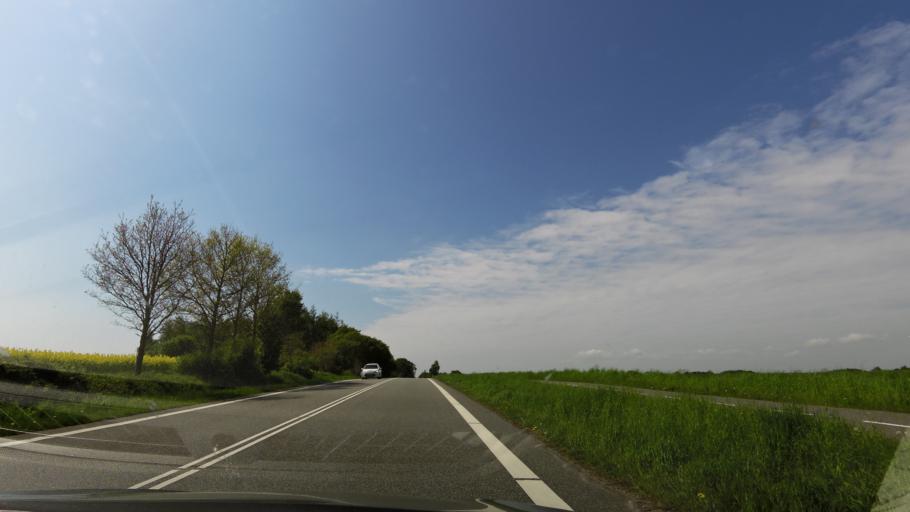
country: DK
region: South Denmark
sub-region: Nyborg Kommune
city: Ullerslev
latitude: 55.2777
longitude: 10.6844
